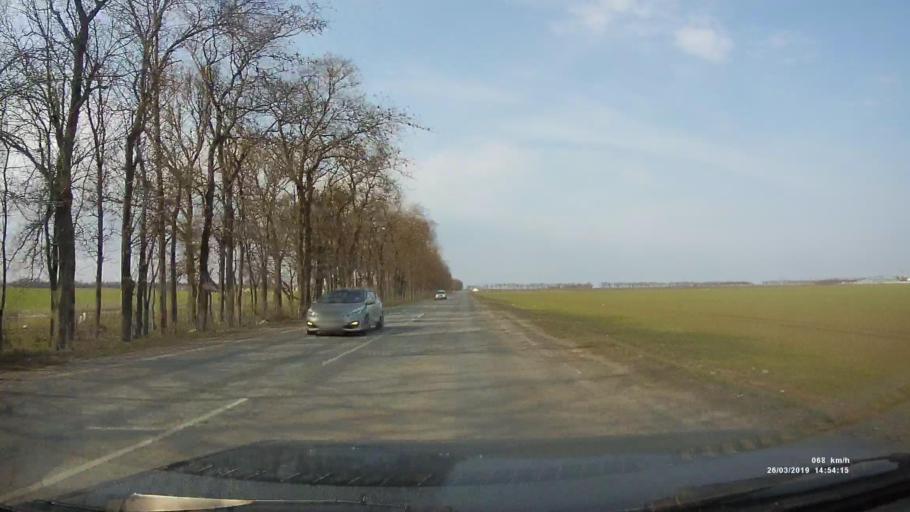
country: RU
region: Rostov
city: Novobessergenovka
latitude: 47.1916
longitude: 38.8142
